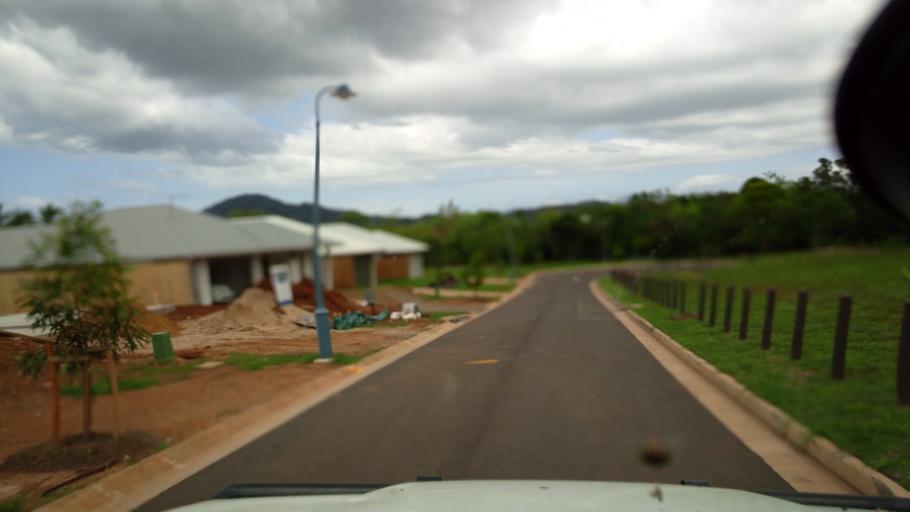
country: AU
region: Queensland
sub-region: Cairns
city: Redlynch
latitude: -16.8984
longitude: 145.6932
